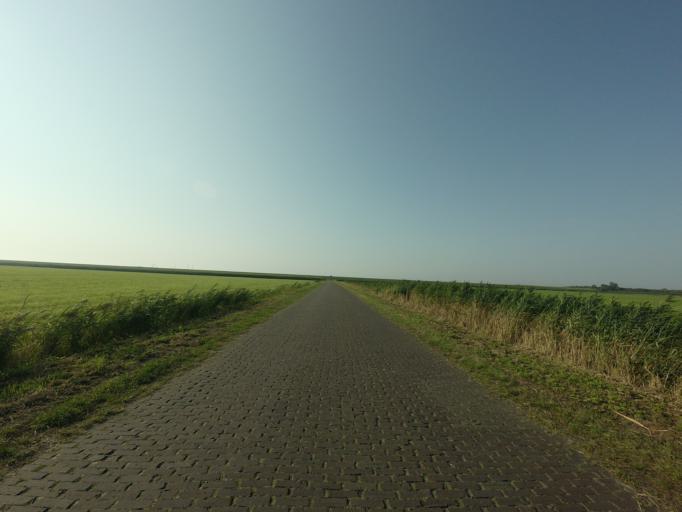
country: NL
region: Friesland
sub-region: Gemeente Schiermonnikoog
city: Schiermonnikoog
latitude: 53.4753
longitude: 6.1617
